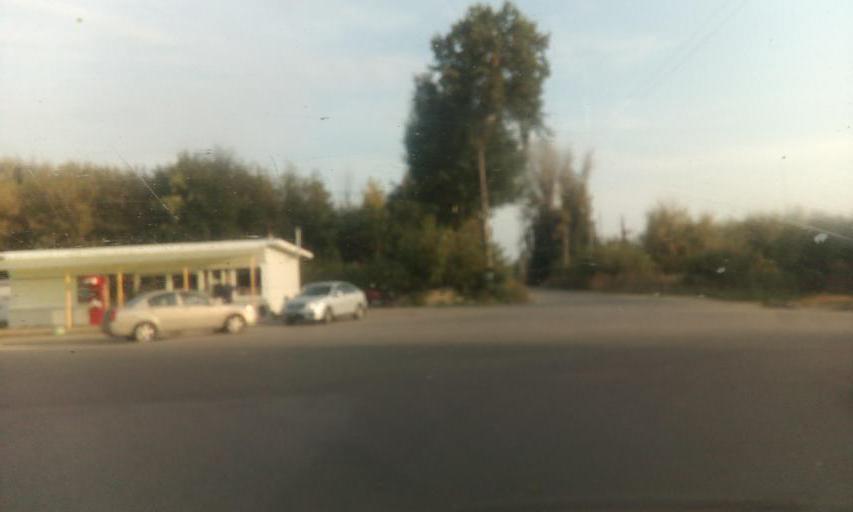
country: RU
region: Tula
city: Partizan
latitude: 53.9230
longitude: 38.1090
